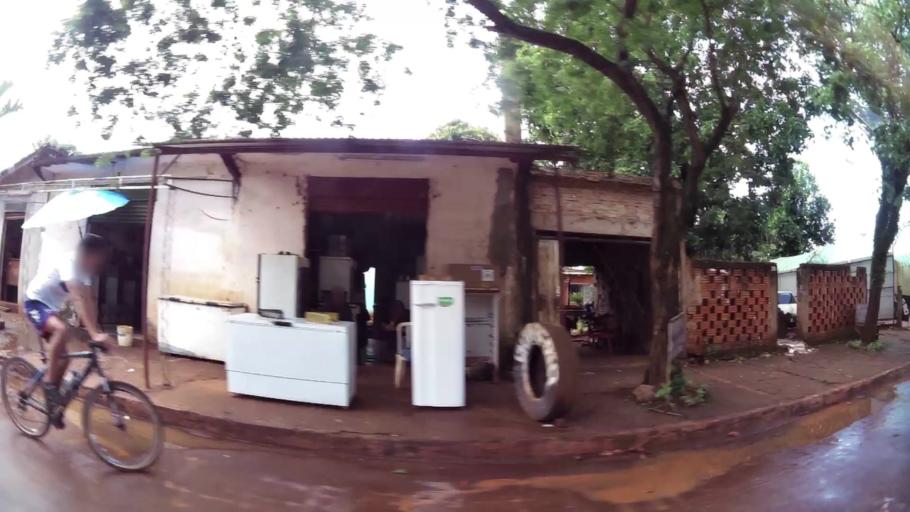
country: PY
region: Alto Parana
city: Ciudad del Este
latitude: -25.5037
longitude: -54.6663
